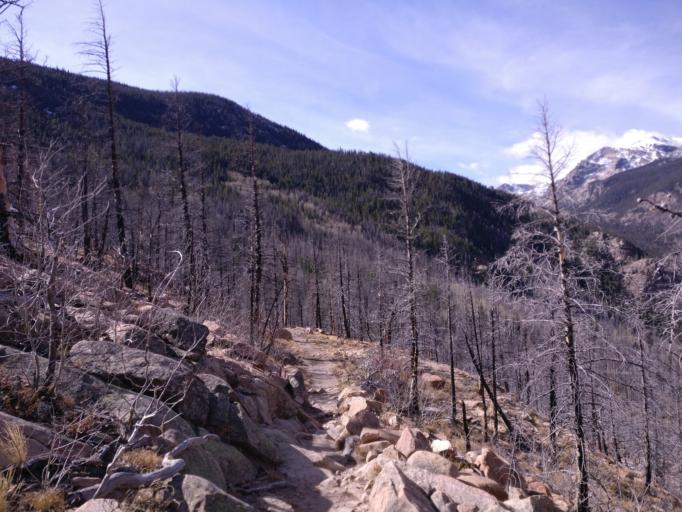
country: US
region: Colorado
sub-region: Larimer County
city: Estes Park
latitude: 40.3473
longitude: -105.6498
